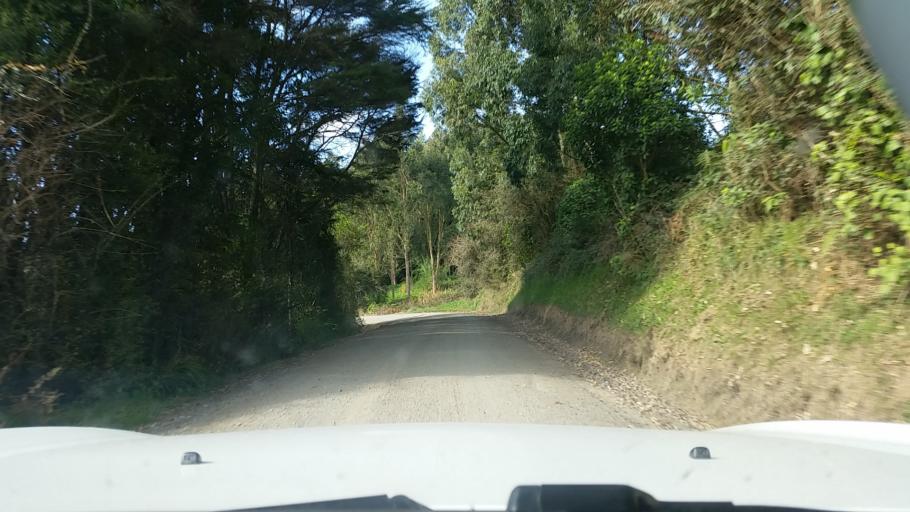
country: NZ
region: Waikato
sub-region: Matamata-Piako District
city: Matamata
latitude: -37.8231
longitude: 175.6362
